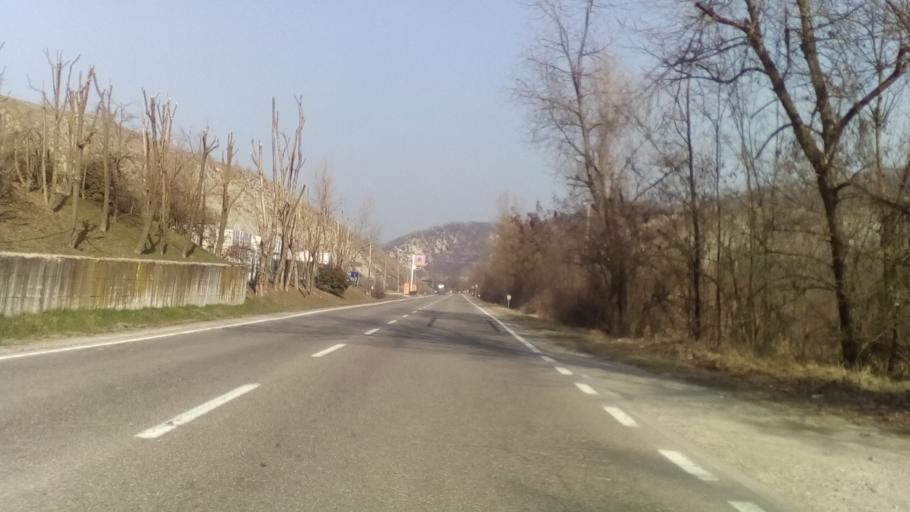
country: IT
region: Emilia-Romagna
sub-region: Provincia di Modena
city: Gorzano
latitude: 44.4705
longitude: 10.8439
